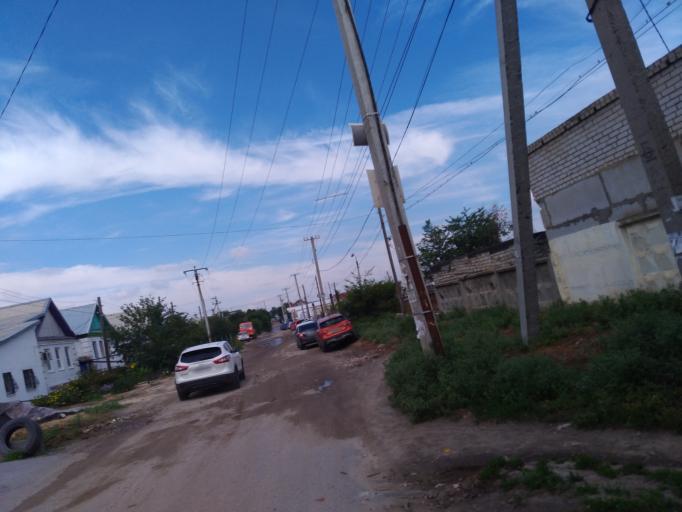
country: RU
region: Volgograd
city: Volgograd
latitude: 48.7112
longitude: 44.4626
